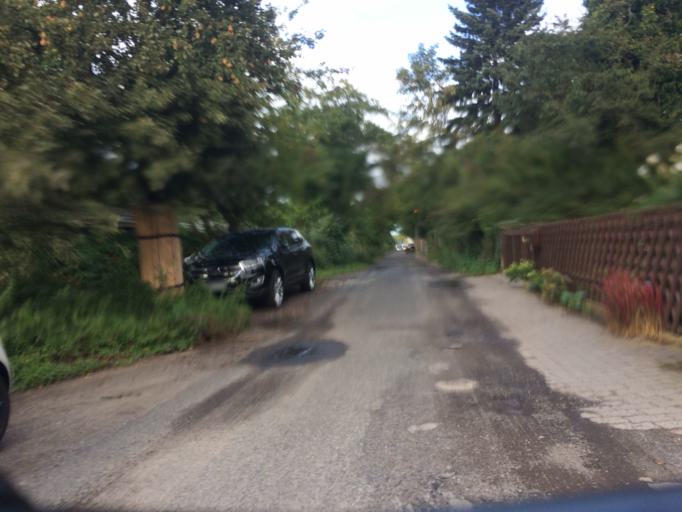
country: DE
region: Berlin
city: Karow
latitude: 52.6126
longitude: 13.4672
